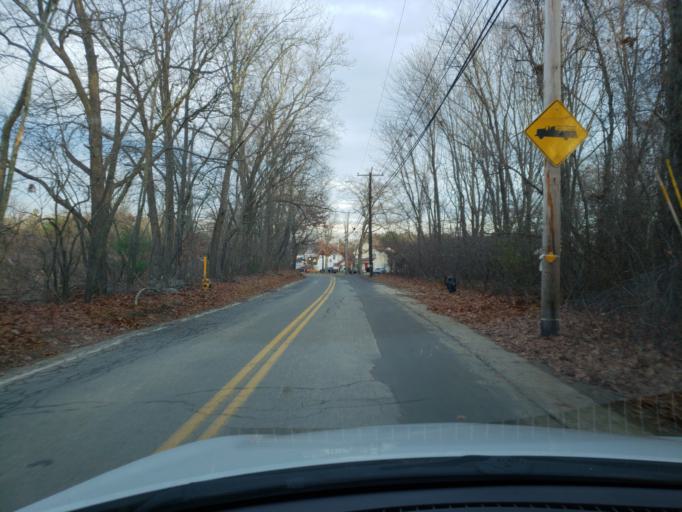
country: US
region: Massachusetts
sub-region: Essex County
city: Lawrence
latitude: 42.6733
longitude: -71.1888
